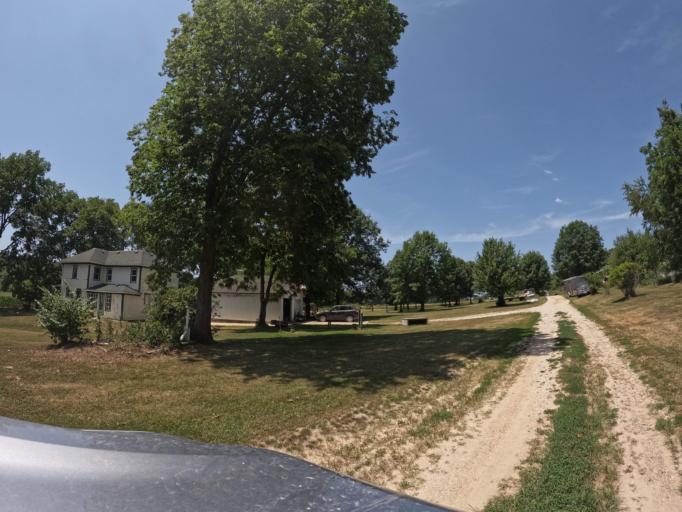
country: US
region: Iowa
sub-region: Henry County
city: Mount Pleasant
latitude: 40.9342
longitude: -91.6028
